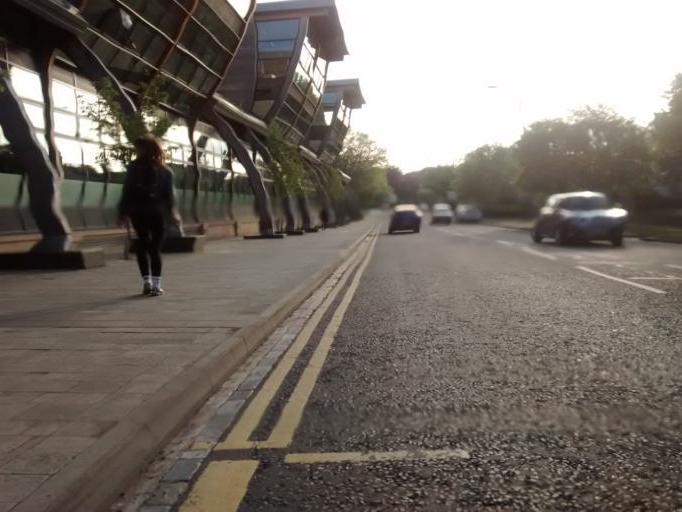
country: GB
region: England
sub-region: County Durham
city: Durham
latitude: 54.7688
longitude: -1.5705
